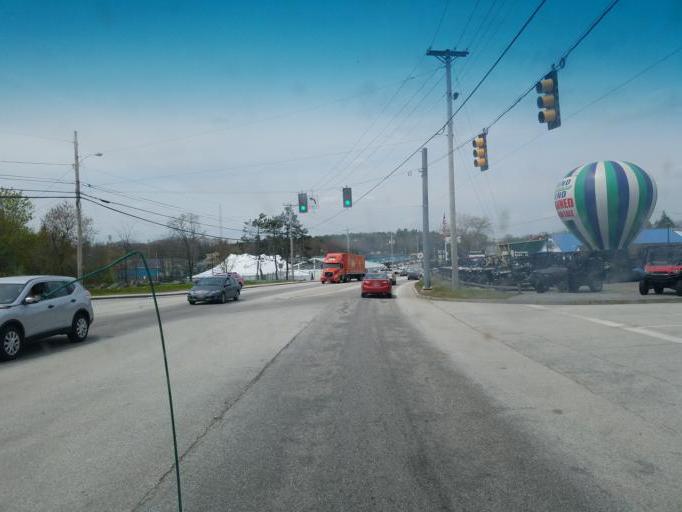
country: US
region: Maine
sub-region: Hancock County
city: Ellsworth
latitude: 44.5500
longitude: -68.4264
